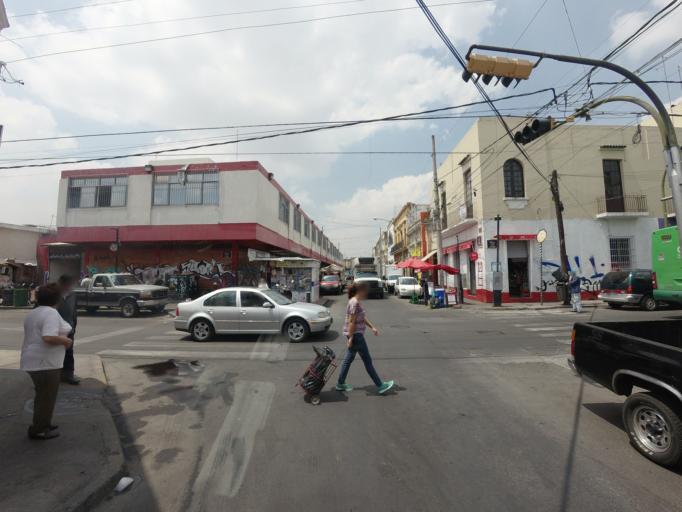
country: MX
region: Jalisco
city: Guadalajara
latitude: 20.6828
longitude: -103.3468
